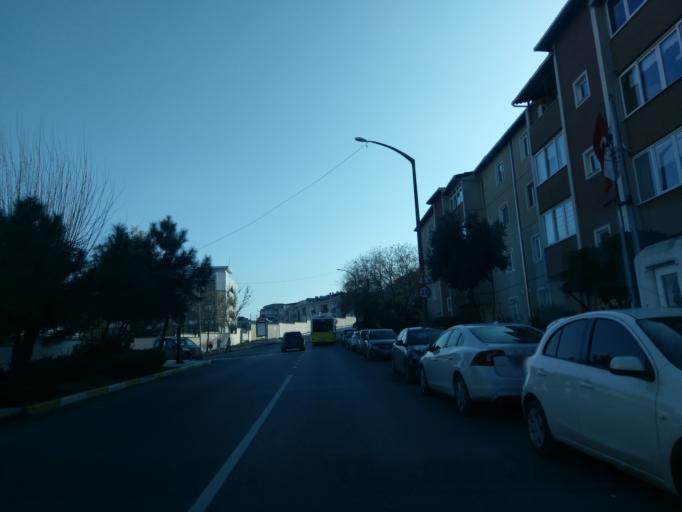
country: TR
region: Istanbul
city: Mahmutbey
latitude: 41.0416
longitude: 28.7961
